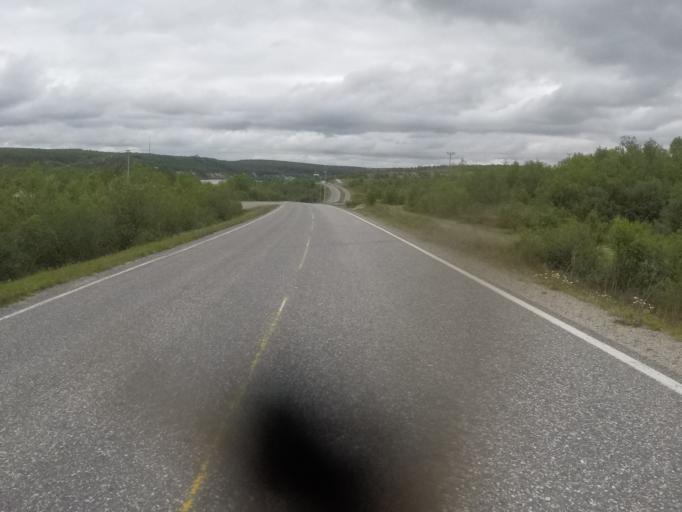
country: NO
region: Finnmark Fylke
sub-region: Kautokeino
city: Kautokeino
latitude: 68.9859
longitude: 23.0522
